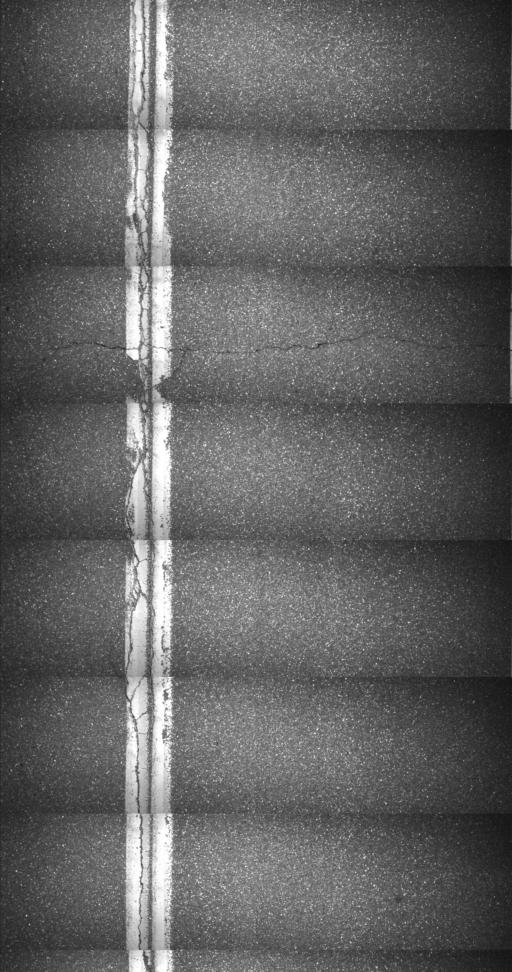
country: US
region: New Hampshire
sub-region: Grafton County
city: Woodsville
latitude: 44.2323
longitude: -72.2318
